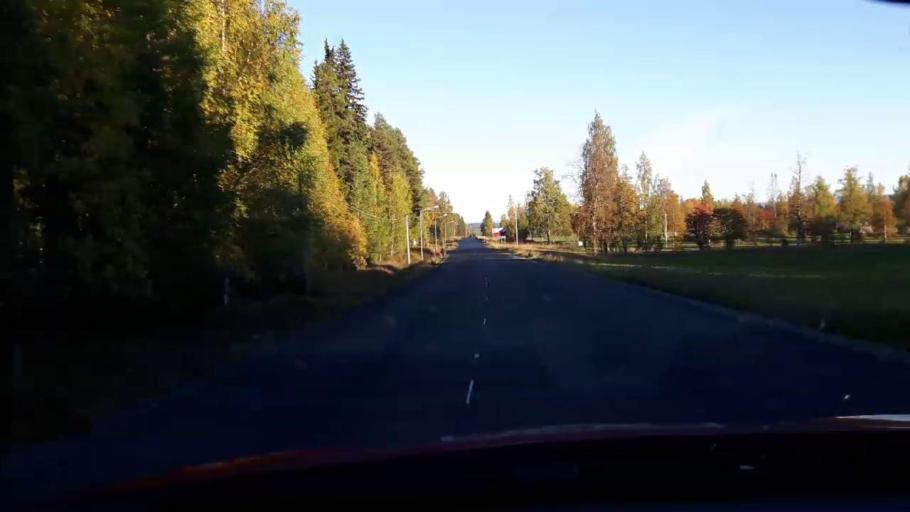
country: SE
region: Jaemtland
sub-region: OEstersunds Kommun
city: Lit
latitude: 63.4022
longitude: 14.8860
